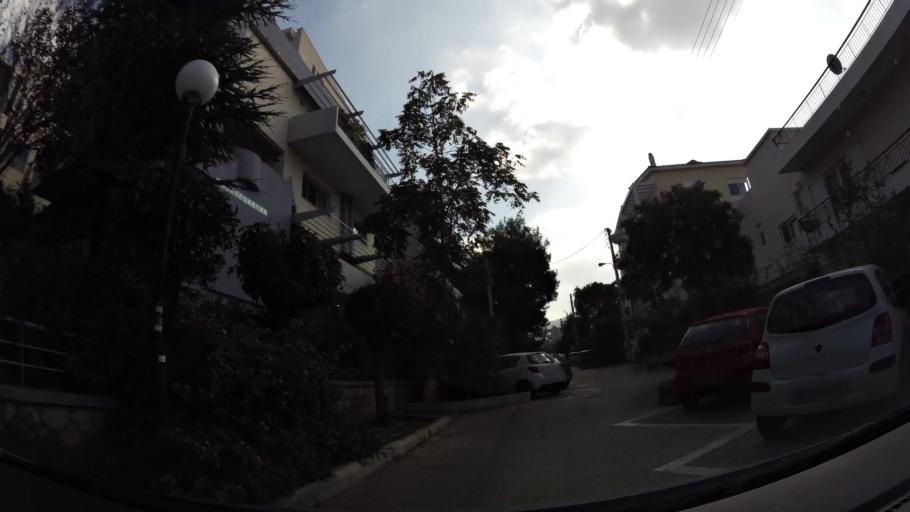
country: GR
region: Attica
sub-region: Nomarchia Athinas
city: Neo Psychiko
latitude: 37.9974
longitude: 23.7887
